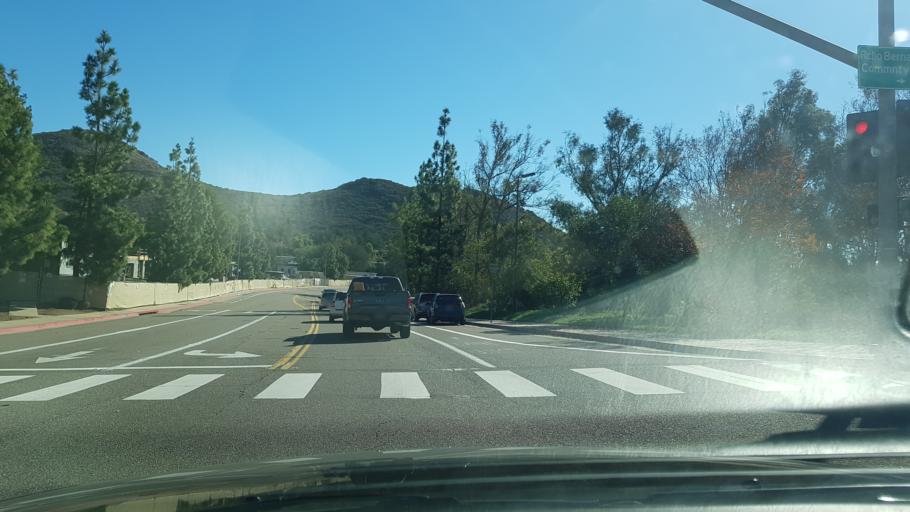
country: US
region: California
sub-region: San Diego County
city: Escondido
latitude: 33.0504
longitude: -117.0755
